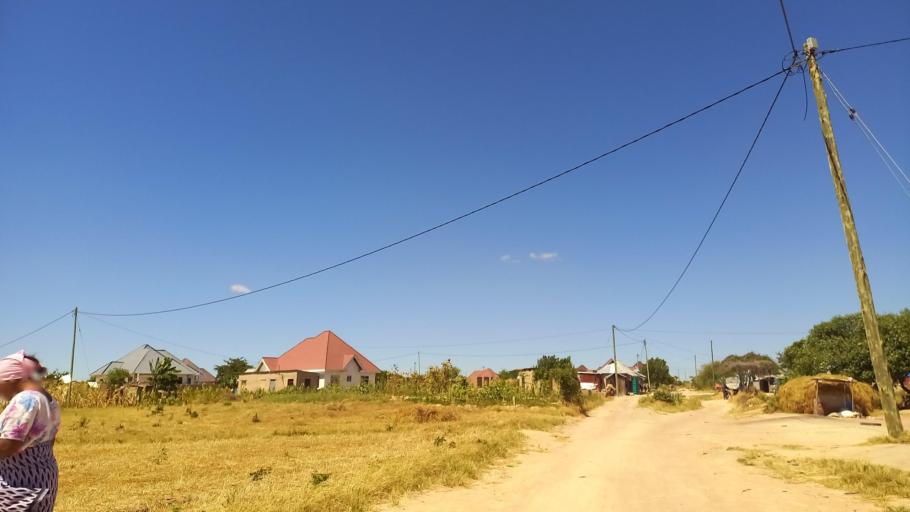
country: TZ
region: Dodoma
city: Dodoma
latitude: -6.1288
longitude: 35.6964
